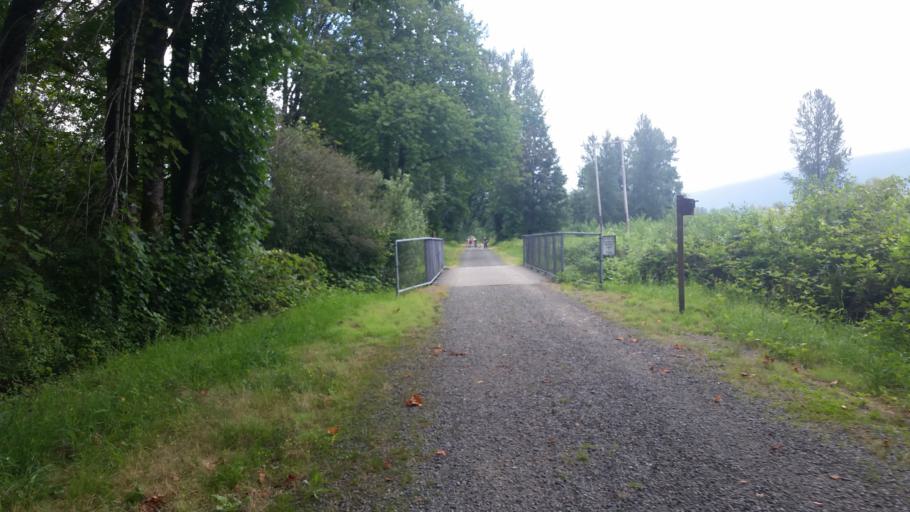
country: US
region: Washington
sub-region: King County
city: Snoqualmie
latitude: 47.5239
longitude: -121.8025
